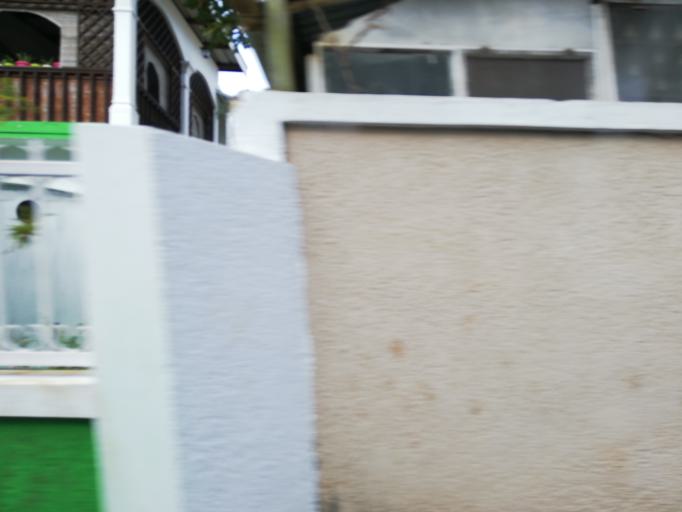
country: MU
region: Black River
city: Petite Riviere
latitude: -20.2200
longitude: 57.4630
